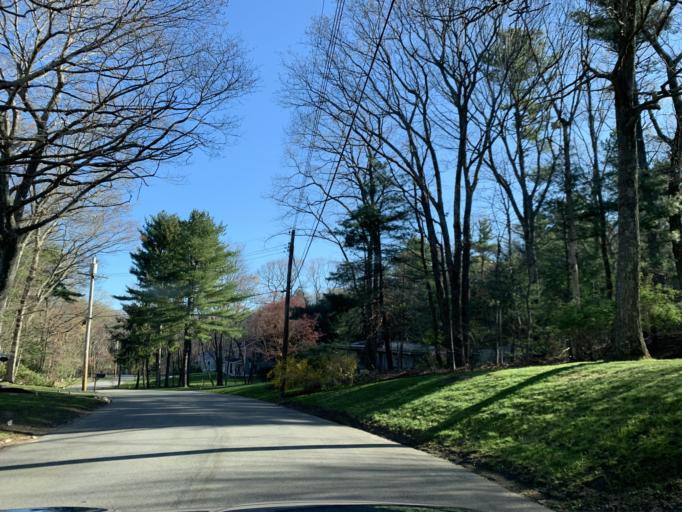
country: US
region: Massachusetts
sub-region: Norfolk County
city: Westwood
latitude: 42.2352
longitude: -71.2021
